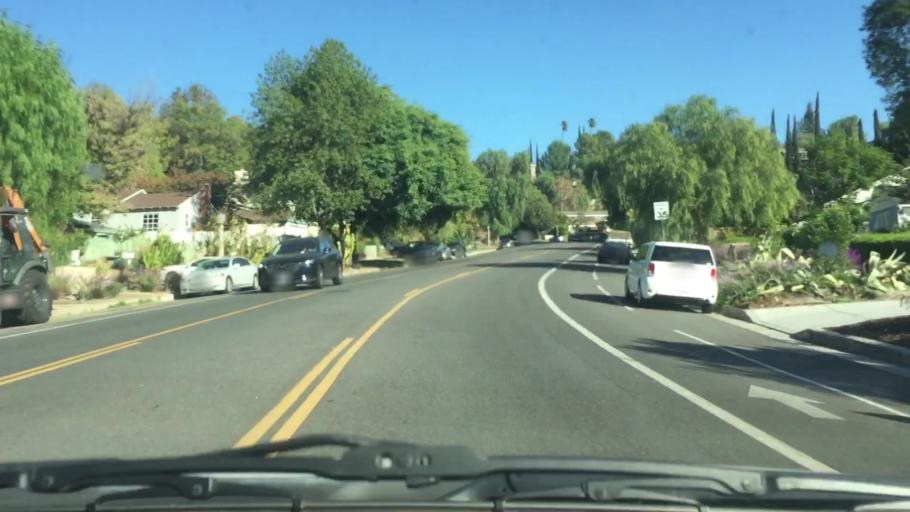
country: US
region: California
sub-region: Los Angeles County
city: Woodland Hills
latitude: 34.1569
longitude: -118.6035
